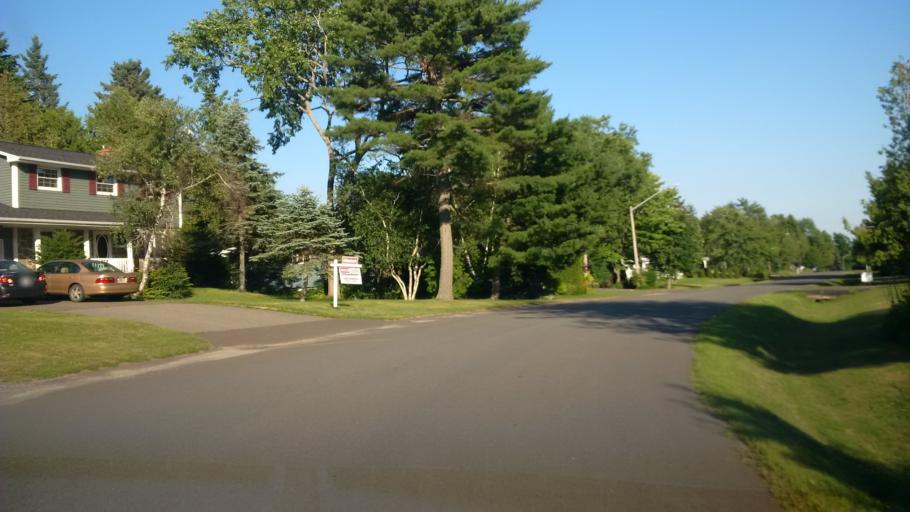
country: CA
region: New Brunswick
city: Fredericton
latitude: 45.8935
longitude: -66.6895
